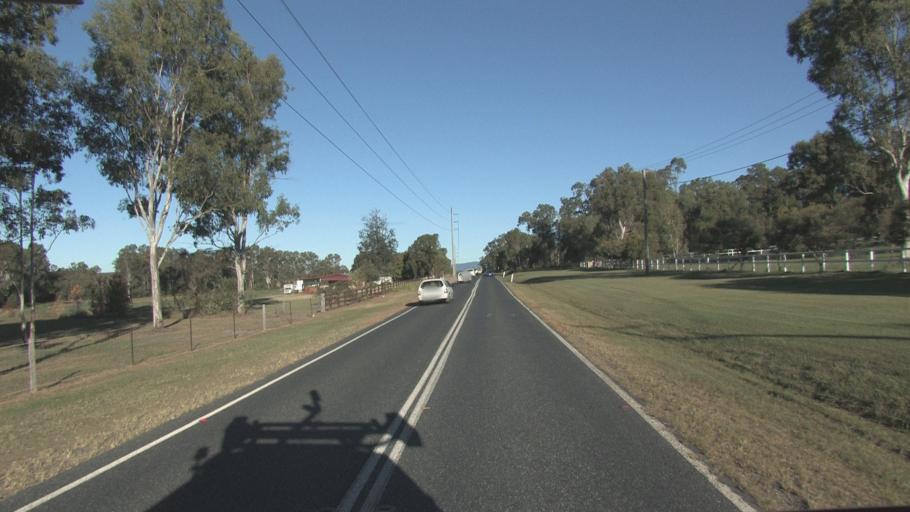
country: AU
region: Queensland
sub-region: Logan
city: Chambers Flat
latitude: -27.7457
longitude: 153.0893
